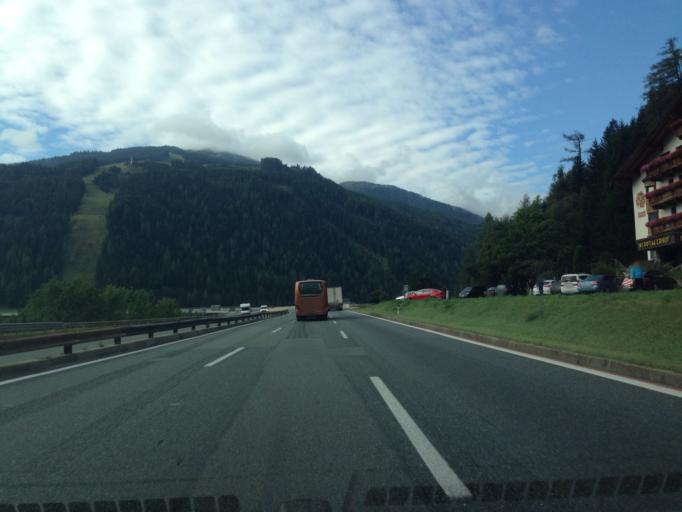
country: AT
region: Tyrol
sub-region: Politischer Bezirk Innsbruck Land
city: Steinach am Brenner
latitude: 47.0925
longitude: 11.4605
